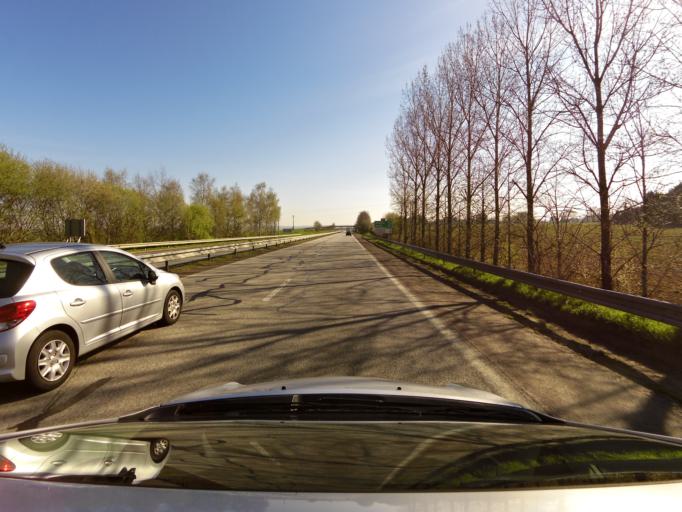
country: FR
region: Brittany
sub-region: Departement du Morbihan
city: Guegon
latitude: 47.9391
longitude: -2.6208
